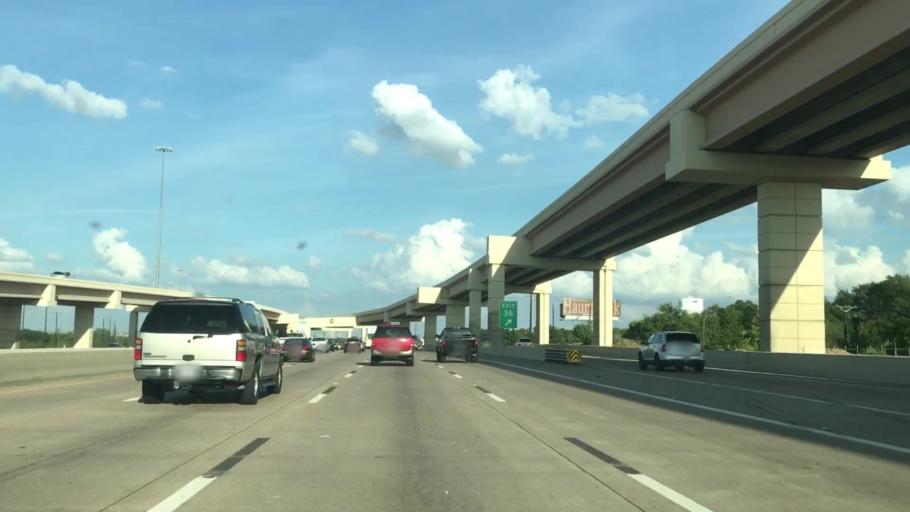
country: US
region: Texas
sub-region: Dallas County
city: Grand Prairie
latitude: 32.7472
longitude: -96.9485
